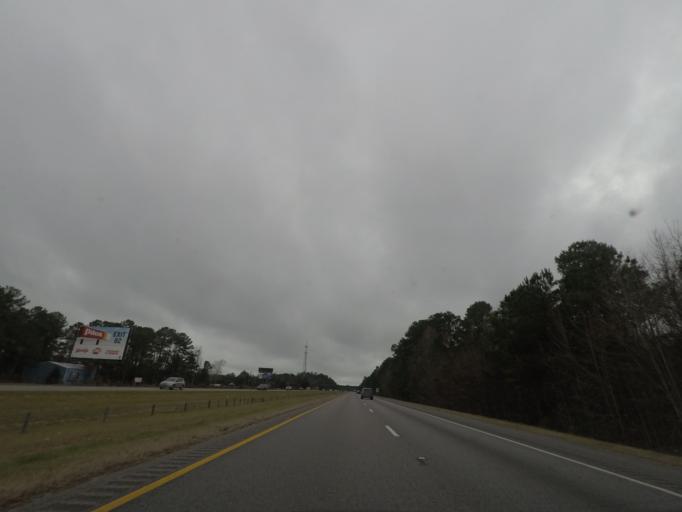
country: US
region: South Carolina
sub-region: Orangeburg County
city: Holly Hill
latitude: 33.4286
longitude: -80.4894
